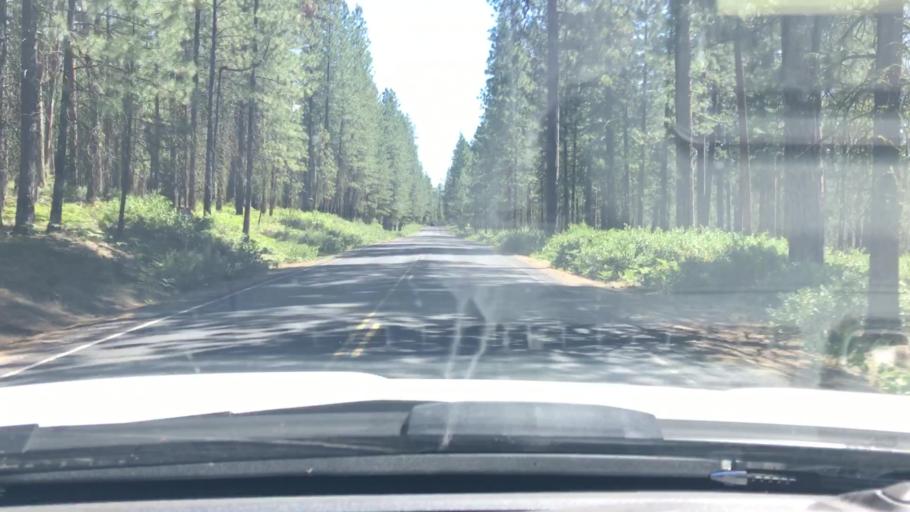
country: US
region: Oregon
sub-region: Deschutes County
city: Sisters
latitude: 44.4086
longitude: -121.6737
